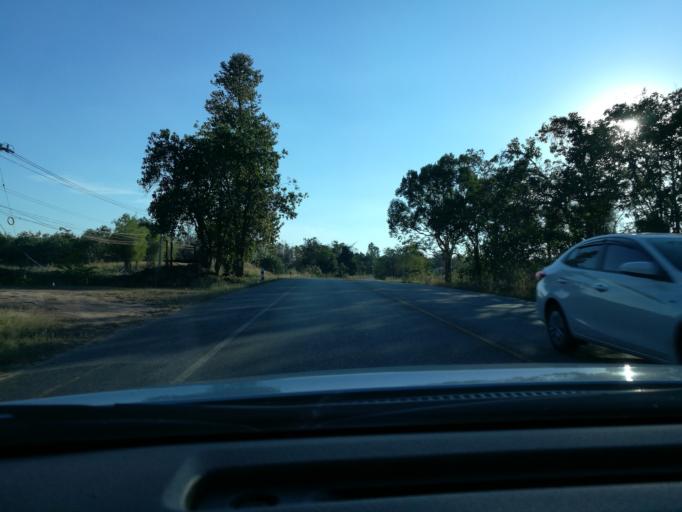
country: TH
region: Phitsanulok
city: Nakhon Thai
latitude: 17.0269
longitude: 100.8168
